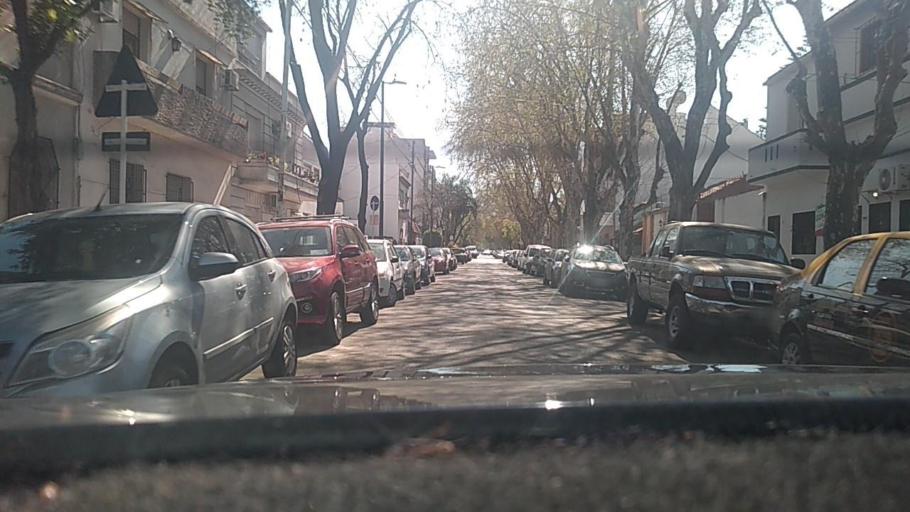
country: AR
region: Buenos Aires F.D.
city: Villa Santa Rita
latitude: -34.6067
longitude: -58.4798
